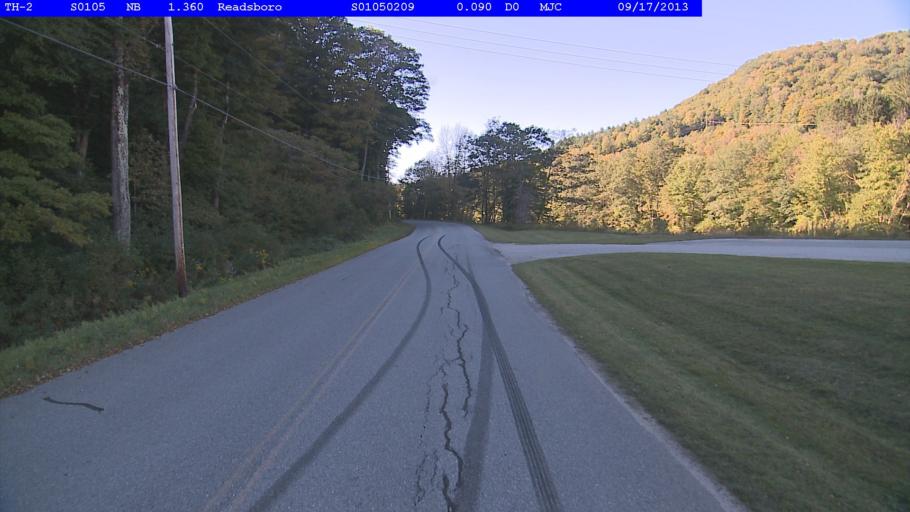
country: US
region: Massachusetts
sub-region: Franklin County
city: Charlemont
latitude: 42.7565
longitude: -72.9310
